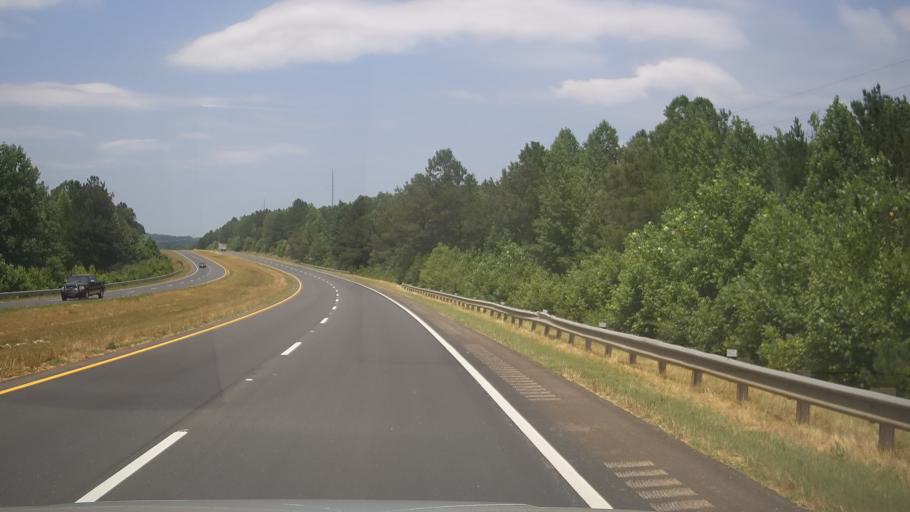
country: US
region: Georgia
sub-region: Jackson County
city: Commerce
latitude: 34.2002
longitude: -83.4326
